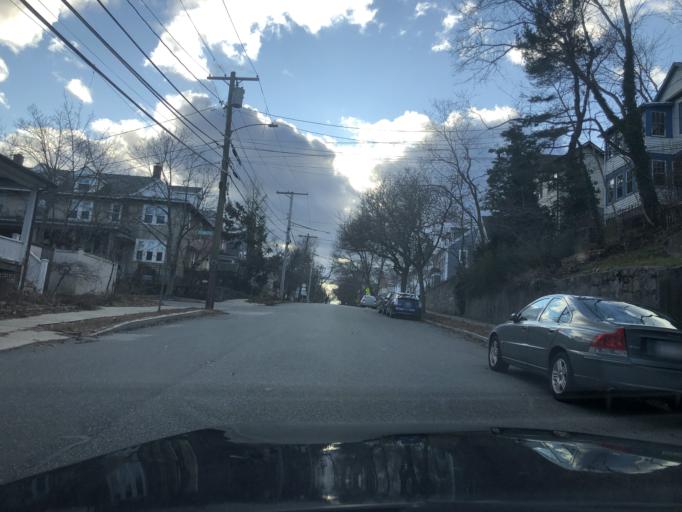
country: US
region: Massachusetts
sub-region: Middlesex County
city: Arlington
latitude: 42.4169
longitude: -71.1663
